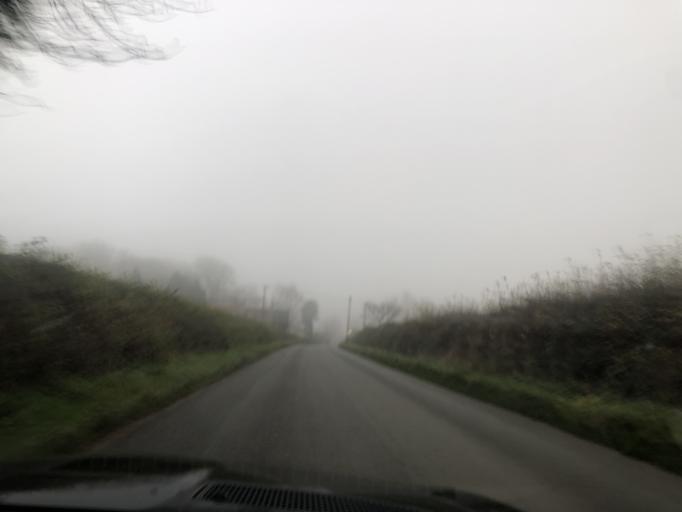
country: GB
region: England
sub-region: Oxfordshire
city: Bicester
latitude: 51.9158
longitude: -1.1756
